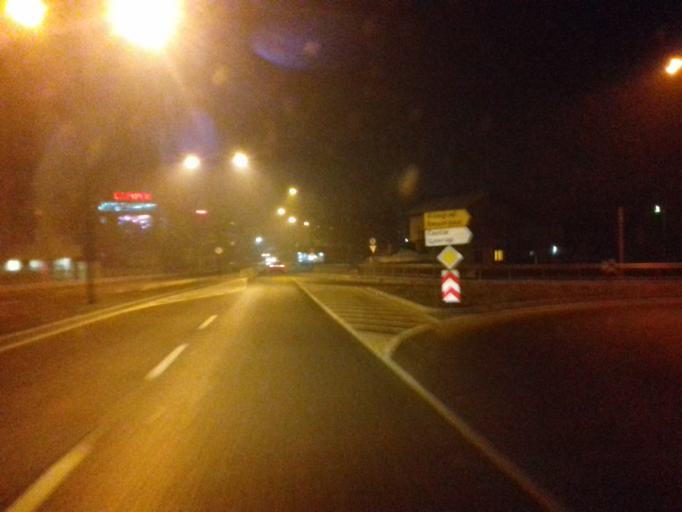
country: BA
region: Federation of Bosnia and Herzegovina
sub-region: Kanton Sarajevo
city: Sarajevo
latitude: 43.8417
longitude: 18.3292
